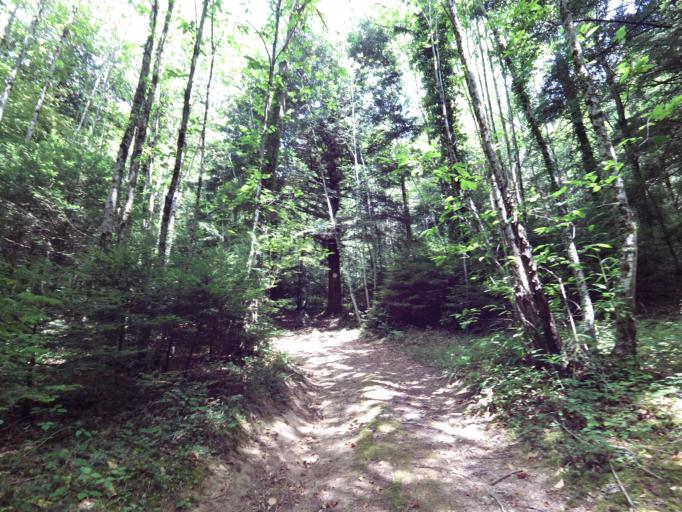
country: IT
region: Calabria
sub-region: Provincia di Vibo-Valentia
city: Mongiana
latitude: 38.5381
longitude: 16.3303
